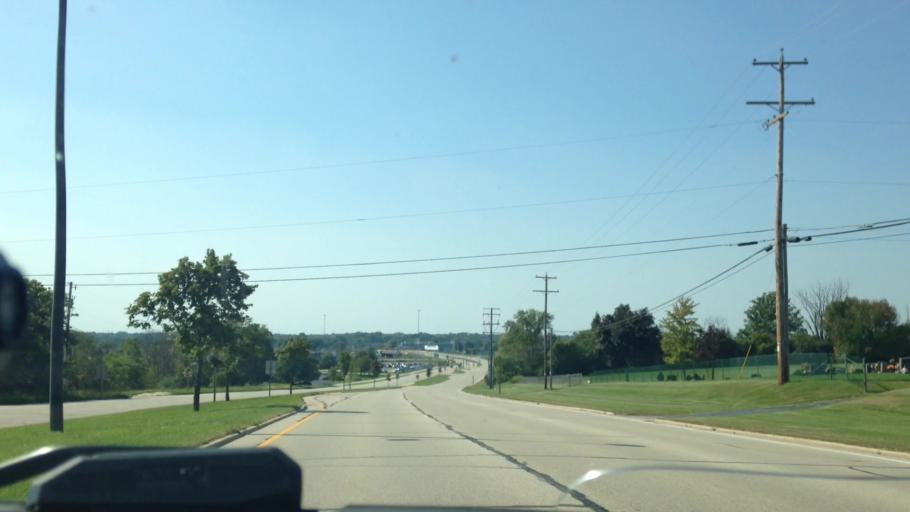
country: US
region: Wisconsin
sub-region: Waukesha County
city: Menomonee Falls
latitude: 43.1773
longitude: -88.0783
